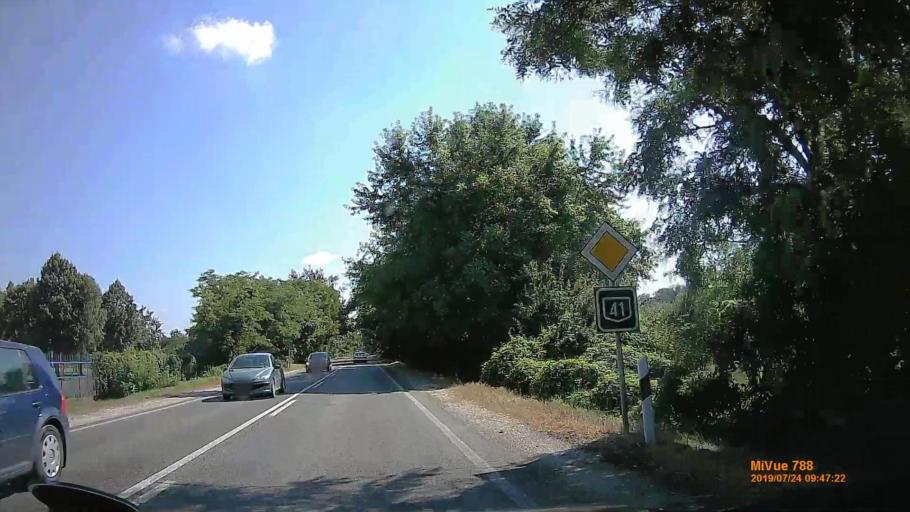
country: HU
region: Szabolcs-Szatmar-Bereg
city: Baktaloranthaza
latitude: 47.9960
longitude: 22.0978
